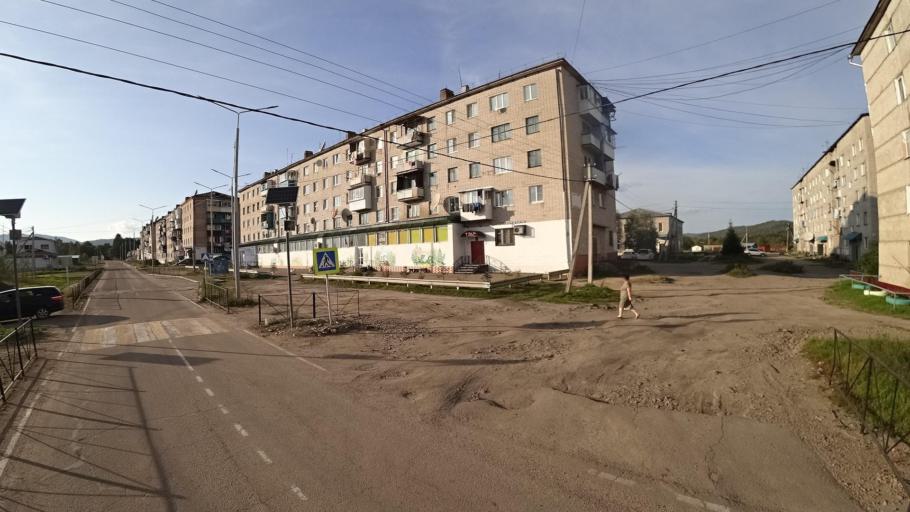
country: RU
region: Jewish Autonomous Oblast
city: Kul'dur
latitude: 49.2015
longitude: 131.6256
